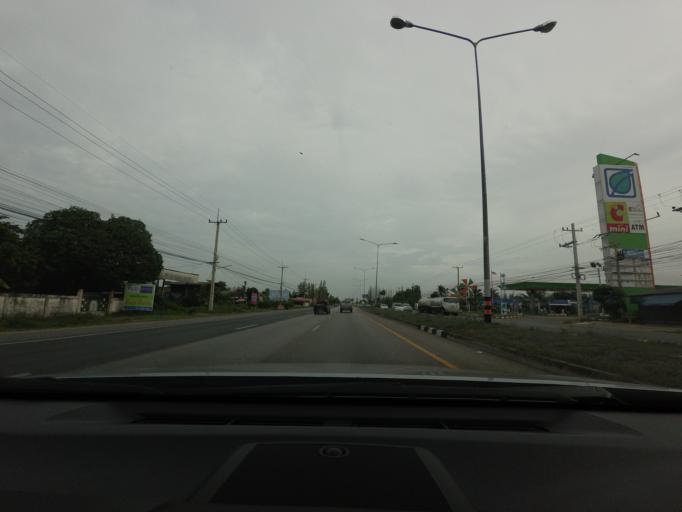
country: TH
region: Phetchaburi
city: Tha Yang
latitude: 12.8924
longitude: 99.9111
